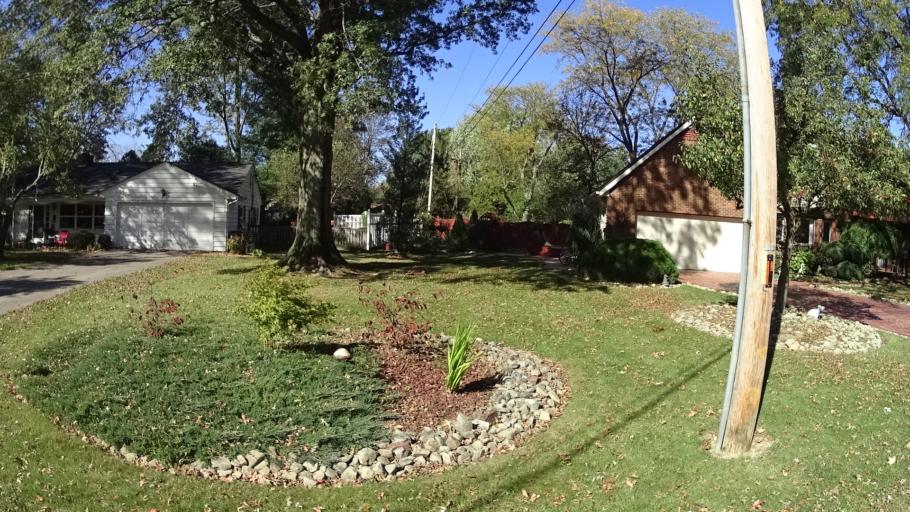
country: US
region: Ohio
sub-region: Lorain County
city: Oberlin
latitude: 41.2920
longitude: -82.2352
